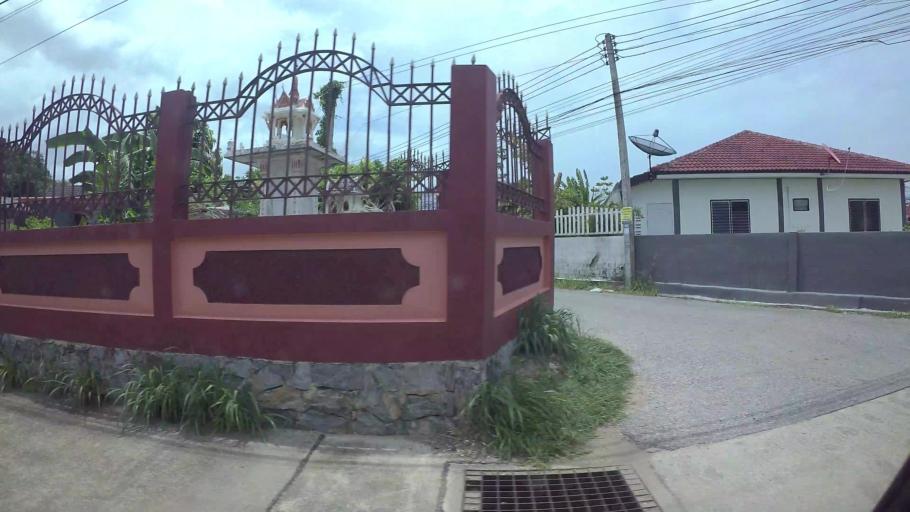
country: TH
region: Chon Buri
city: Sattahip
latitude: 12.6839
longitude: 100.9024
